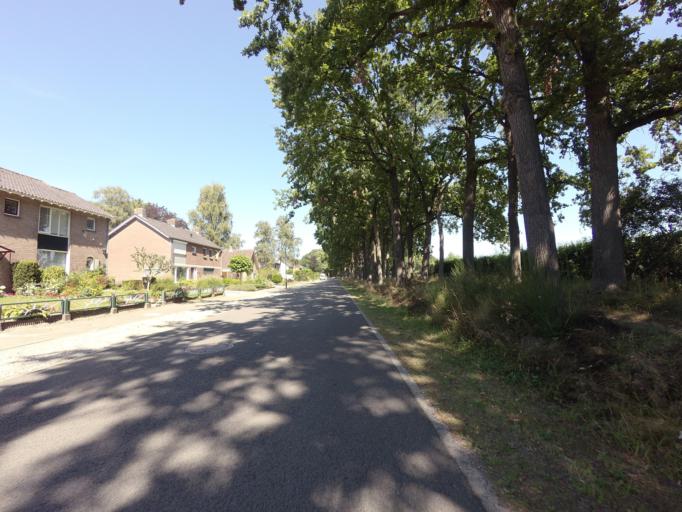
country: NL
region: Gelderland
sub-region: Gemeente Apeldoorn
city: Loenen
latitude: 52.1173
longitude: 6.0244
